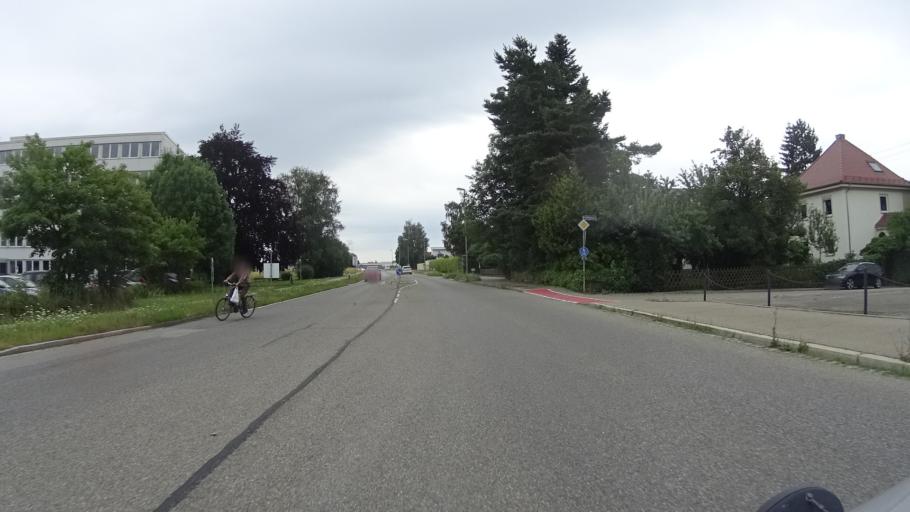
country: DE
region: Bavaria
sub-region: Swabia
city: Heimertingen
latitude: 48.0122
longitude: 10.1646
